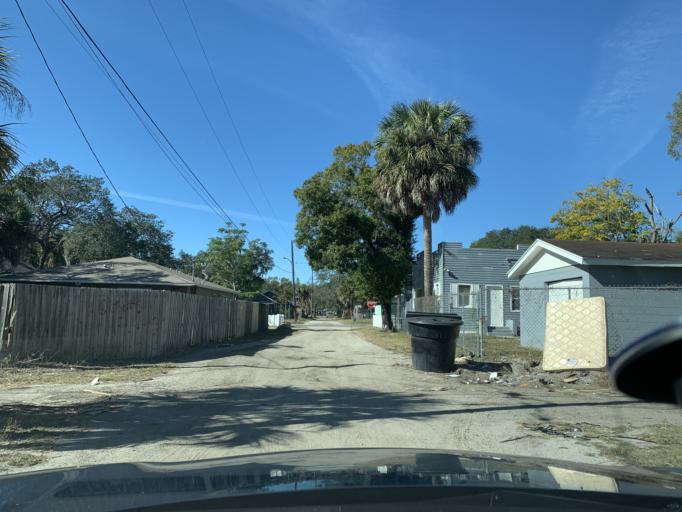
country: US
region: Florida
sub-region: Pinellas County
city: Gulfport
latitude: 27.7501
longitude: -82.6925
